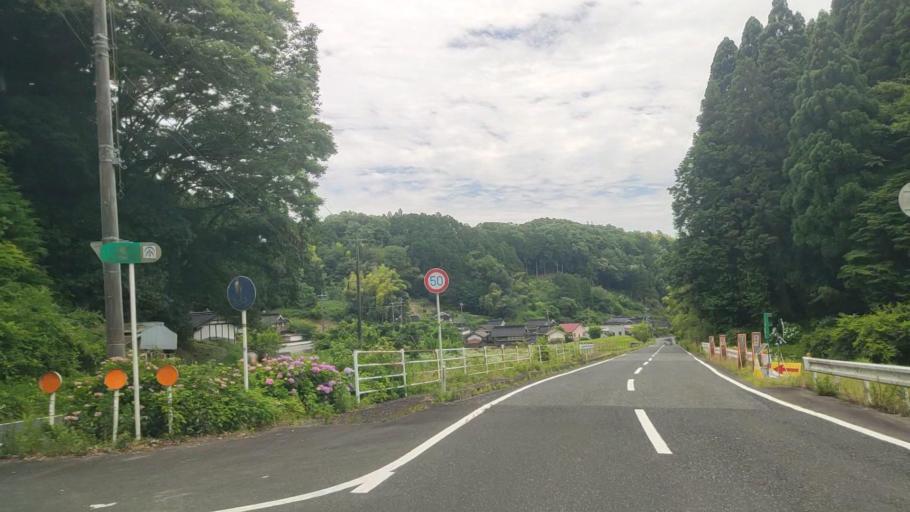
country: JP
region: Hyogo
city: Yamazakicho-nakabirose
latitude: 35.0972
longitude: 134.2812
